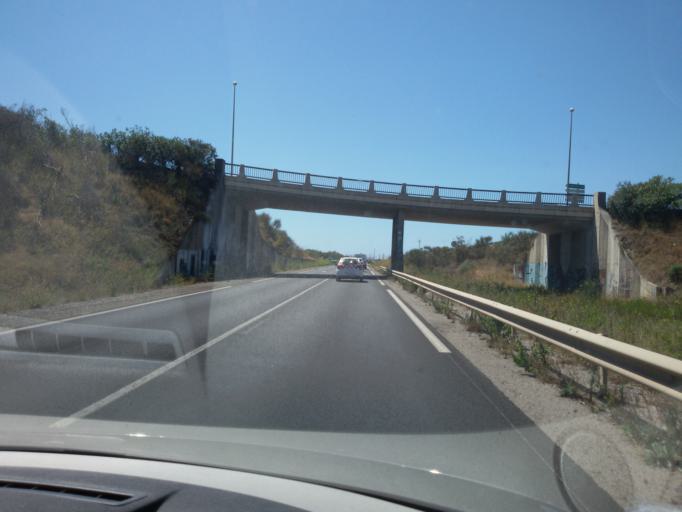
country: FR
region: Languedoc-Roussillon
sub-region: Departement de l'Herault
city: Frontignan
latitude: 43.4377
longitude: 3.7613
